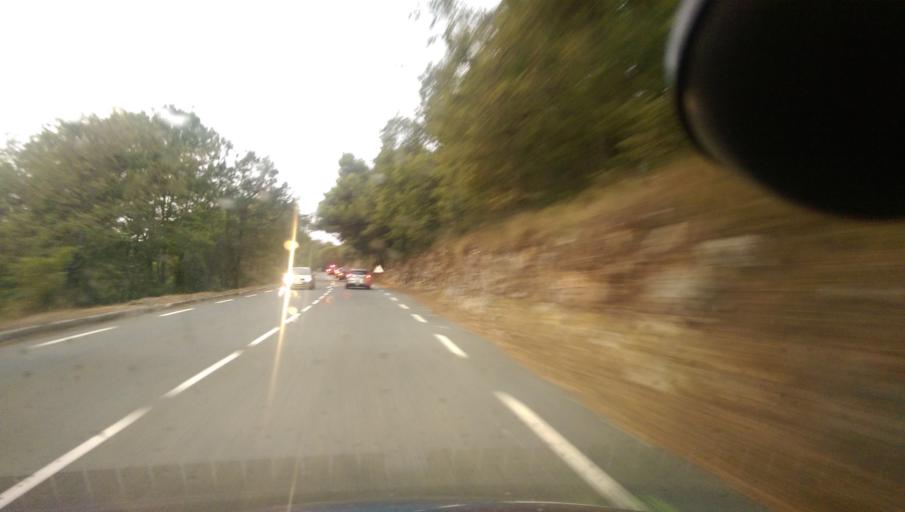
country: FR
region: Provence-Alpes-Cote d'Azur
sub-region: Departement des Alpes-Maritimes
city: Grasse
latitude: 43.6816
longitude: 6.8908
